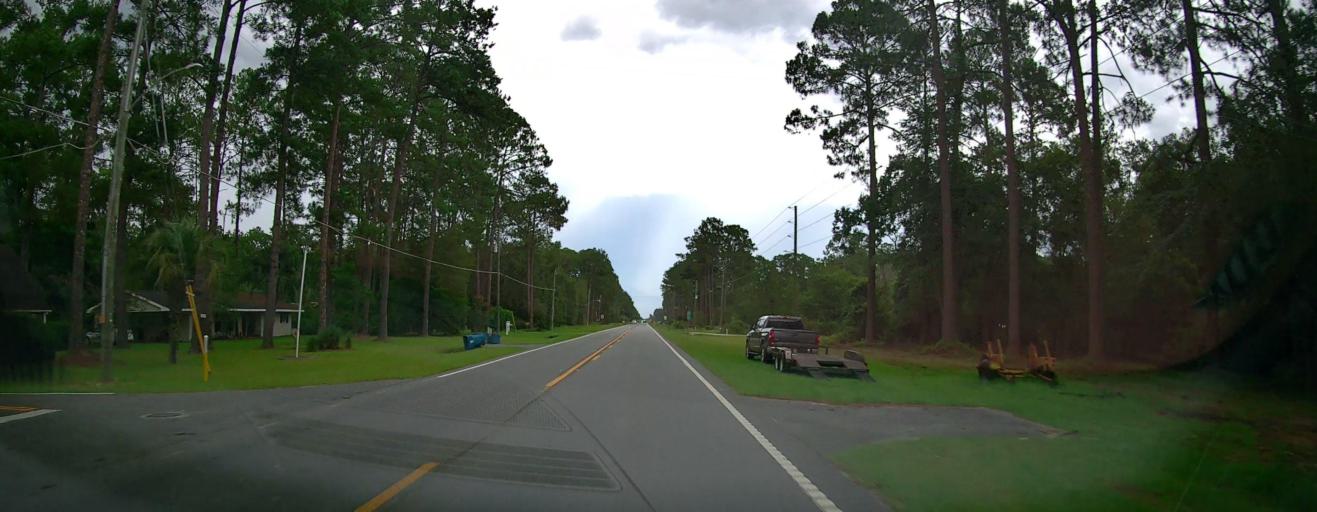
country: US
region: Georgia
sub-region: Pierce County
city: Blackshear
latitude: 31.3790
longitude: -82.1293
